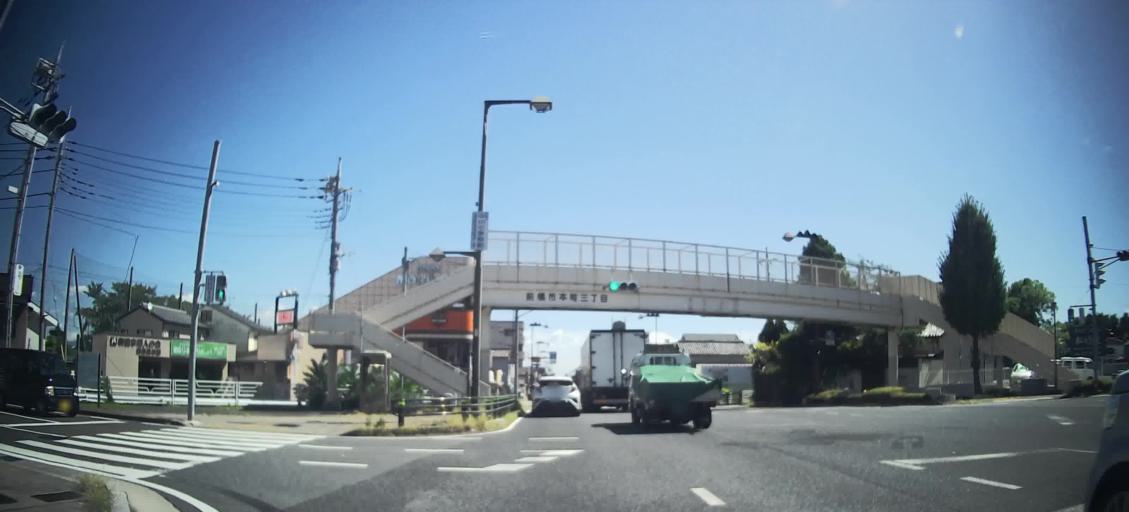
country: JP
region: Gunma
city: Maebashi-shi
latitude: 36.3856
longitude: 139.0773
